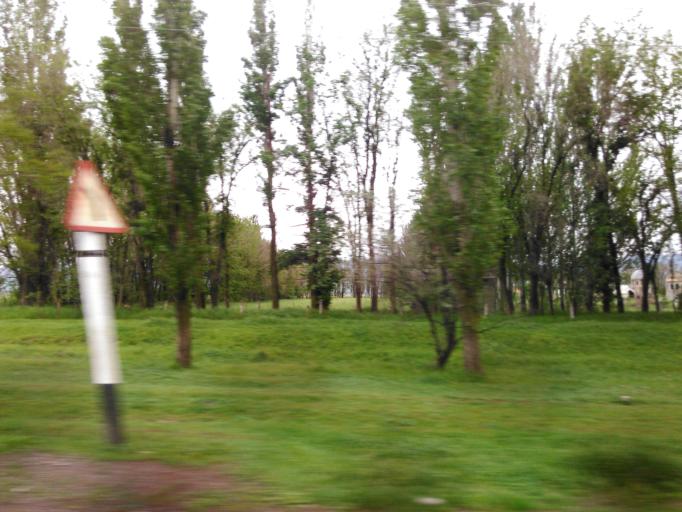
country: KG
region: Chuy
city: Chuy
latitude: 42.7472
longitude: 75.2708
